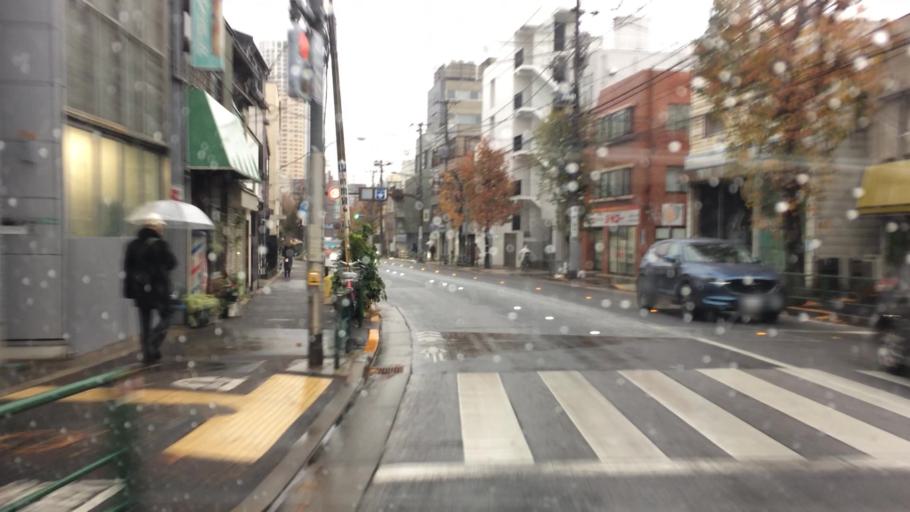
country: JP
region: Tokyo
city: Tokyo
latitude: 35.6382
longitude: 139.6975
